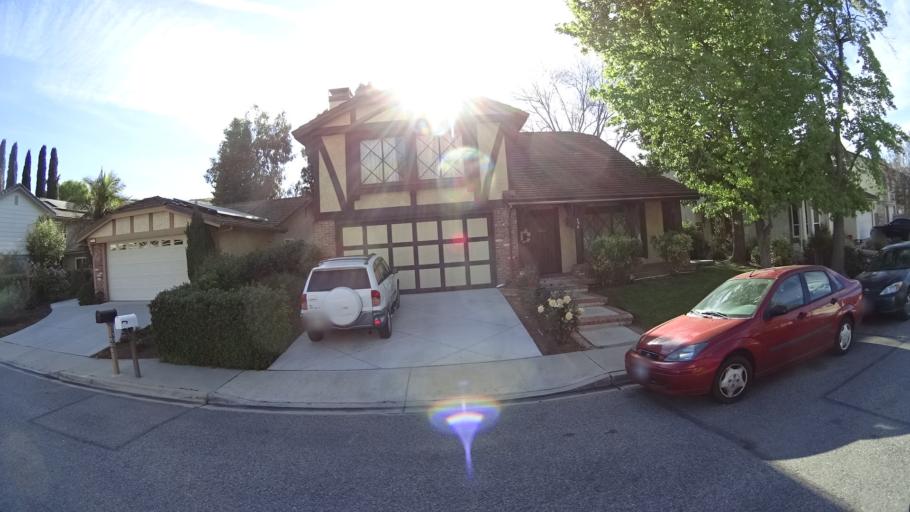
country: US
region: California
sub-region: Ventura County
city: Casa Conejo
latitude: 34.1920
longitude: -118.9593
